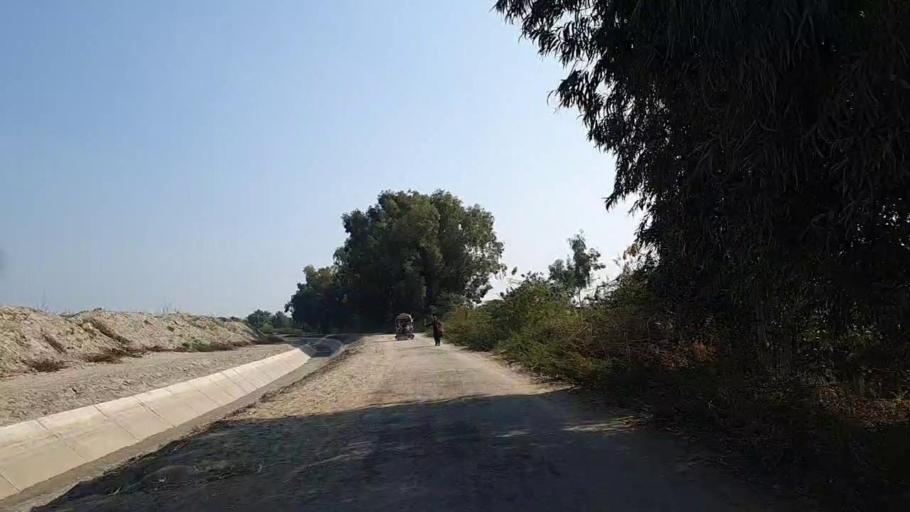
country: PK
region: Sindh
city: Jam Sahib
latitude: 26.2738
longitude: 68.5564
